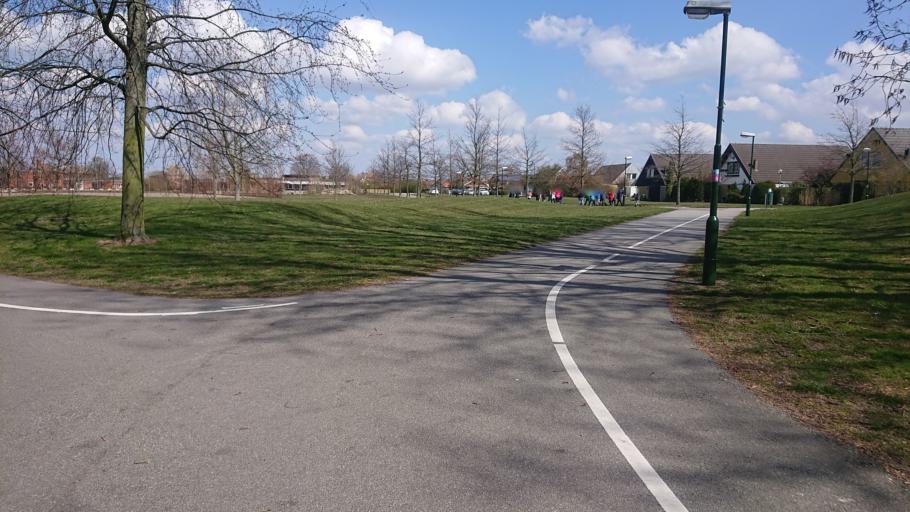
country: SE
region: Skane
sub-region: Malmo
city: Bunkeflostrand
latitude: 55.5717
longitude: 12.9524
